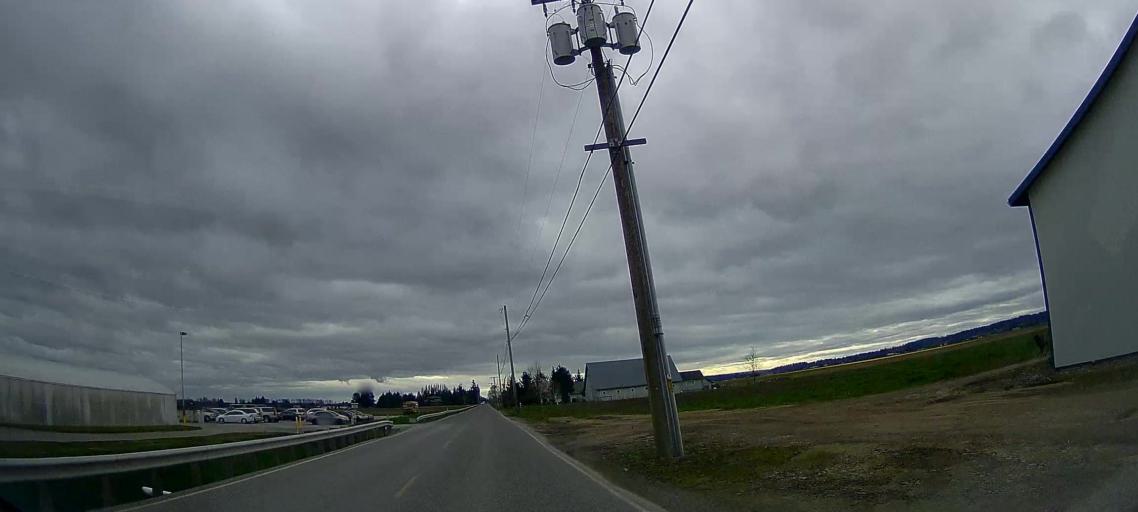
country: US
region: Washington
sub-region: Skagit County
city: Mount Vernon
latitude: 48.4115
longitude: -122.4011
